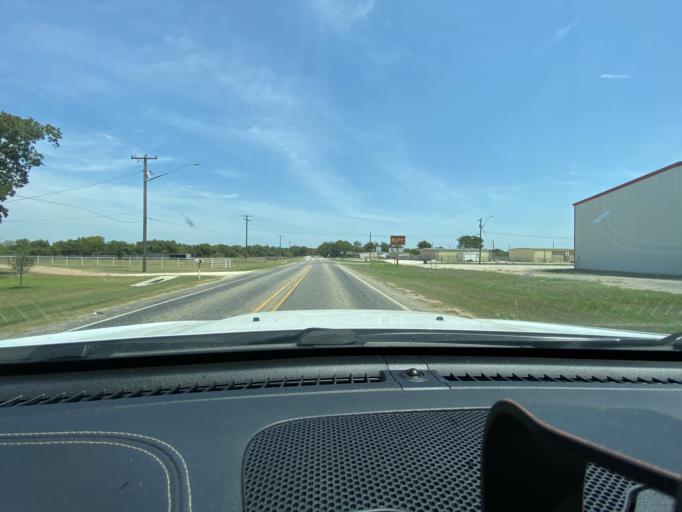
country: US
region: Texas
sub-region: Lee County
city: Giddings
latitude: 30.1693
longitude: -96.9406
